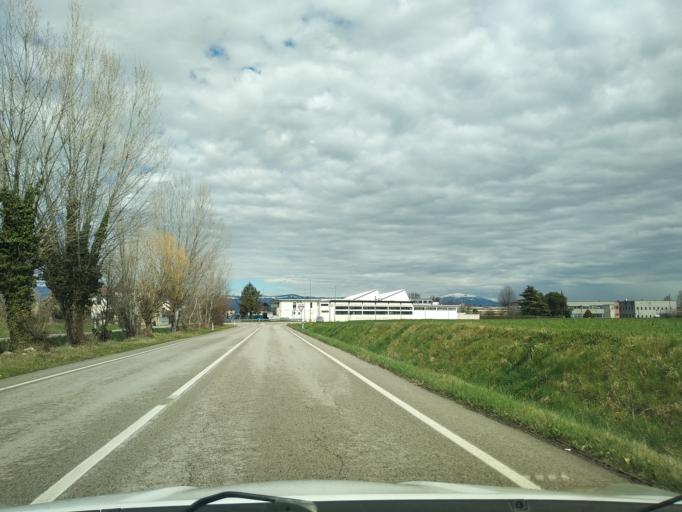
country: IT
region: Veneto
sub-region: Provincia di Vicenza
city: Monticello Conte Otto
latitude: 45.5880
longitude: 11.5791
